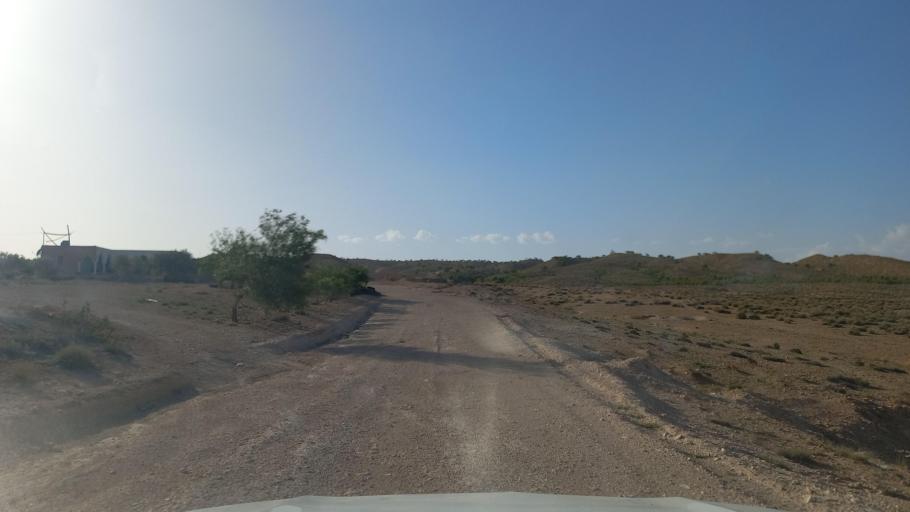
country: TN
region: Al Qasrayn
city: Sbiba
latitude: 35.3645
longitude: 8.9989
